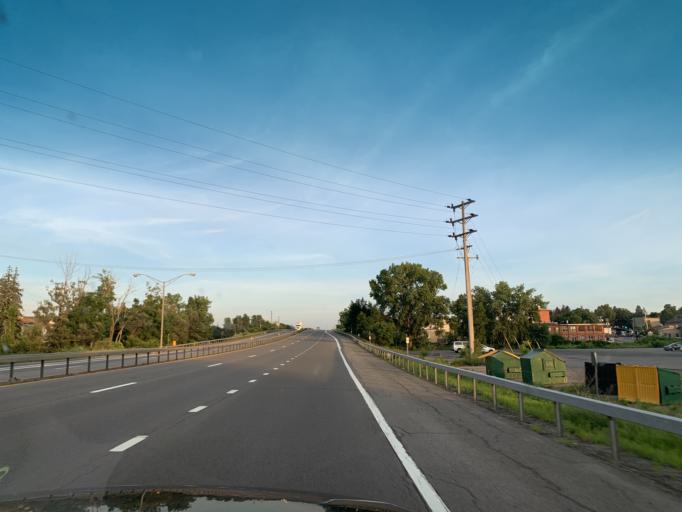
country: US
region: New York
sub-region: Oneida County
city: New Hartford
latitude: 43.0766
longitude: -75.2881
